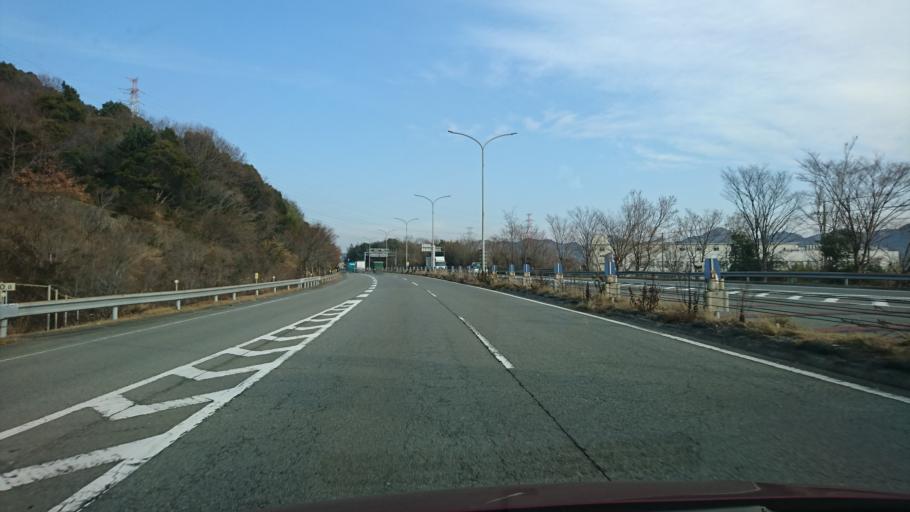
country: JP
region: Hyogo
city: Shirahamacho-usazakiminami
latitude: 34.8031
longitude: 134.7435
